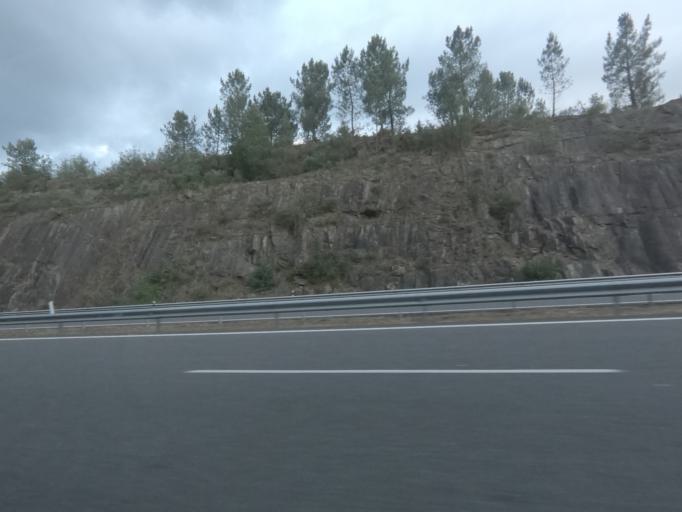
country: ES
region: Galicia
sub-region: Provincia de Ourense
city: Carballeda de Avia
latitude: 42.3066
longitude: -8.1557
